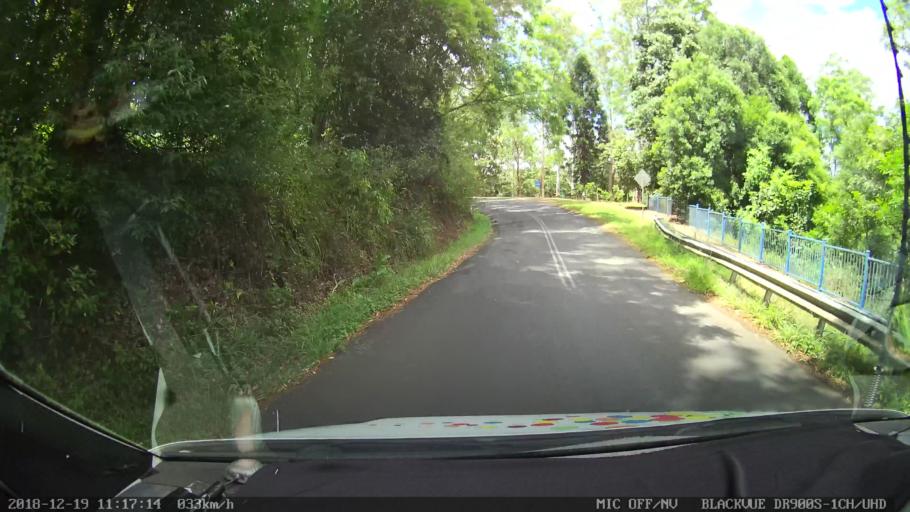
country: AU
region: New South Wales
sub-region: Lismore Municipality
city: Nimbin
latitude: -28.6778
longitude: 153.2797
